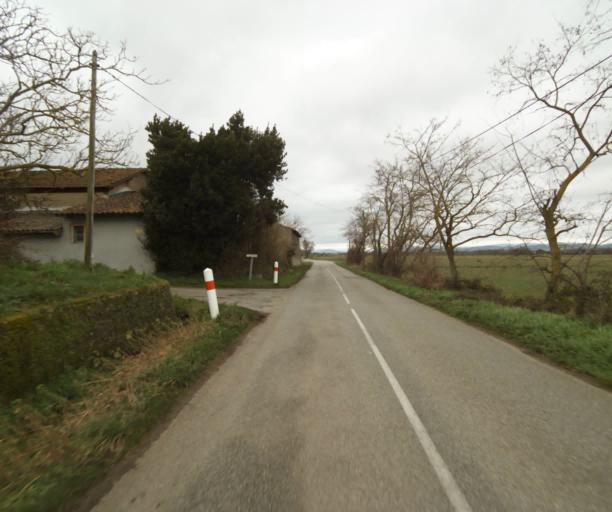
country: FR
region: Midi-Pyrenees
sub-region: Departement de l'Ariege
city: Pamiers
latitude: 43.1849
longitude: 1.6346
